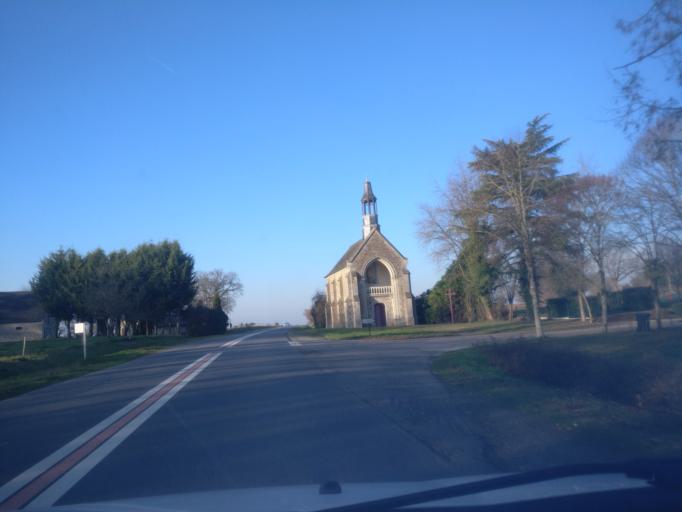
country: FR
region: Brittany
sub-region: Departement d'Ille-et-Vilaine
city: Livre-sur-Changeon
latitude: 48.2014
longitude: -1.3324
